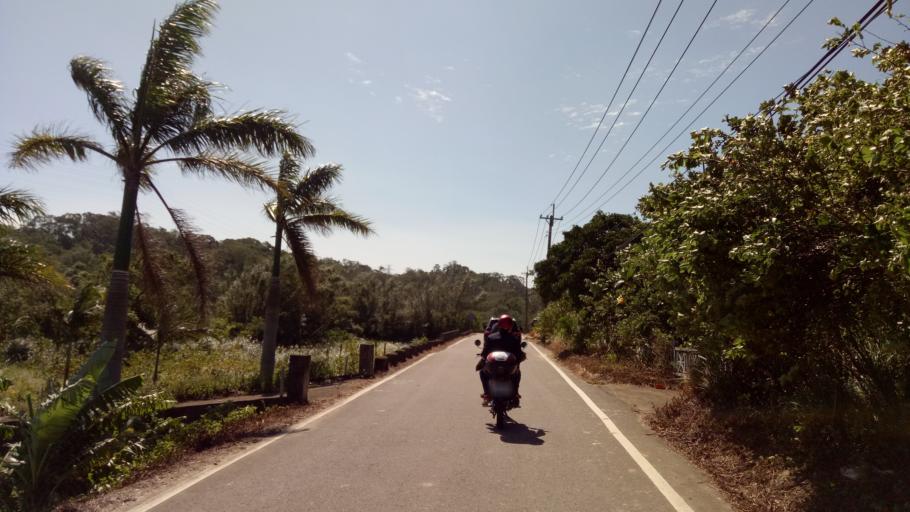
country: TW
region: Taiwan
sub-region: Hsinchu
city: Hsinchu
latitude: 24.7363
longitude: 120.9482
